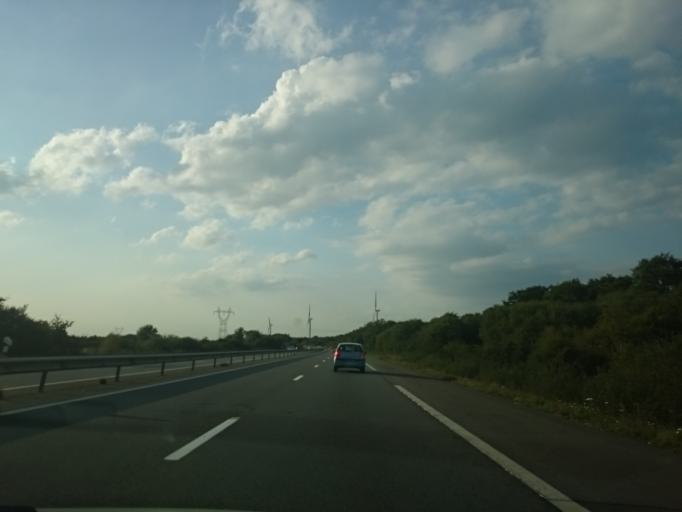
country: FR
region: Pays de la Loire
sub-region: Departement de la Loire-Atlantique
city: Prinquiau
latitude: 47.4019
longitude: -2.0080
